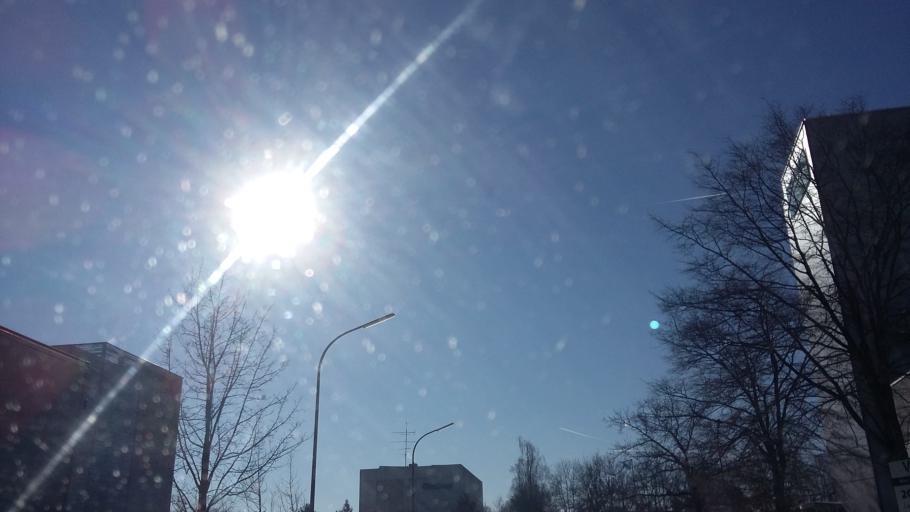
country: DE
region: Bavaria
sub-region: Upper Bavaria
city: Grafelfing
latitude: 48.1086
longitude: 11.4329
